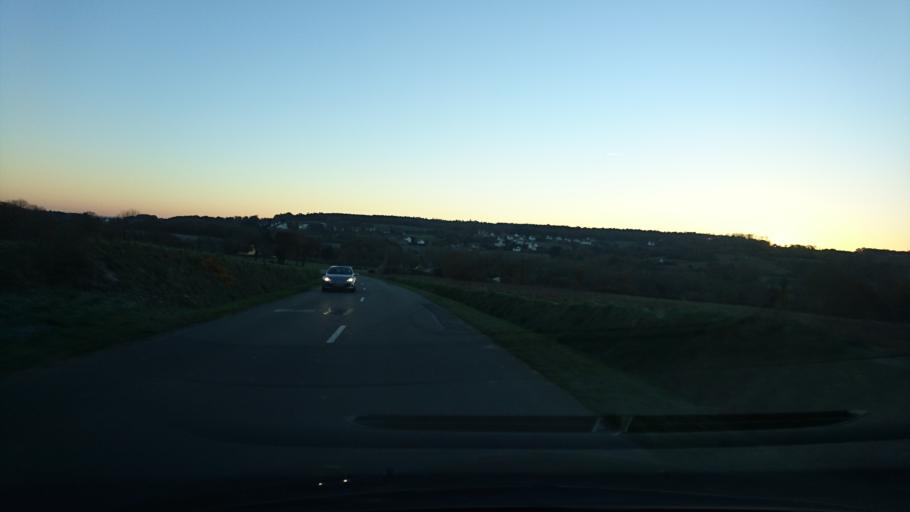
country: FR
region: Brittany
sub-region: Departement des Cotes-d'Armor
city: Pledran
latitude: 48.4586
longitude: -2.7689
